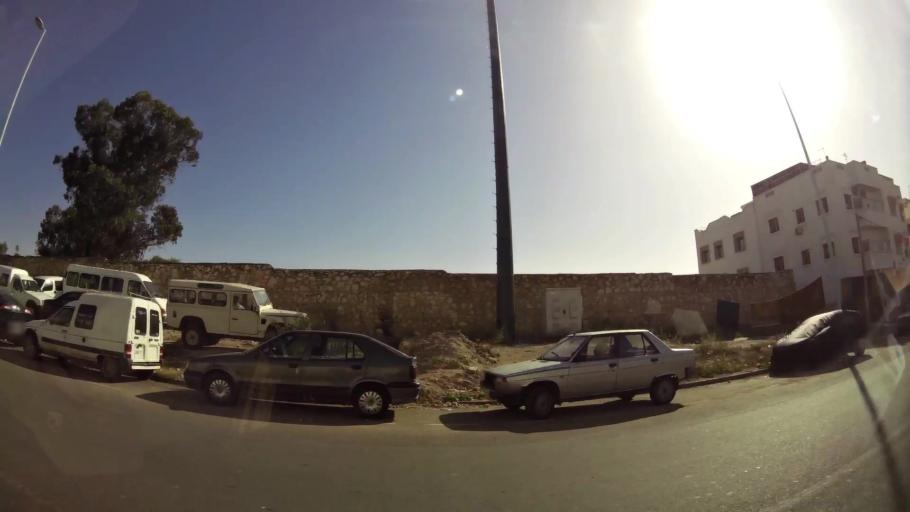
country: MA
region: Oued ed Dahab-Lagouira
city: Dakhla
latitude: 30.4184
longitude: -9.5684
